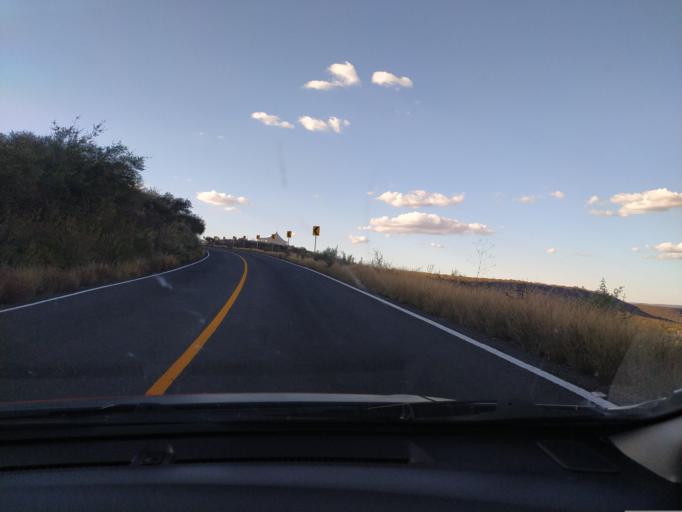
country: MX
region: Guanajuato
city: San Francisco del Rincon
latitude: 21.0290
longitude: -101.8998
